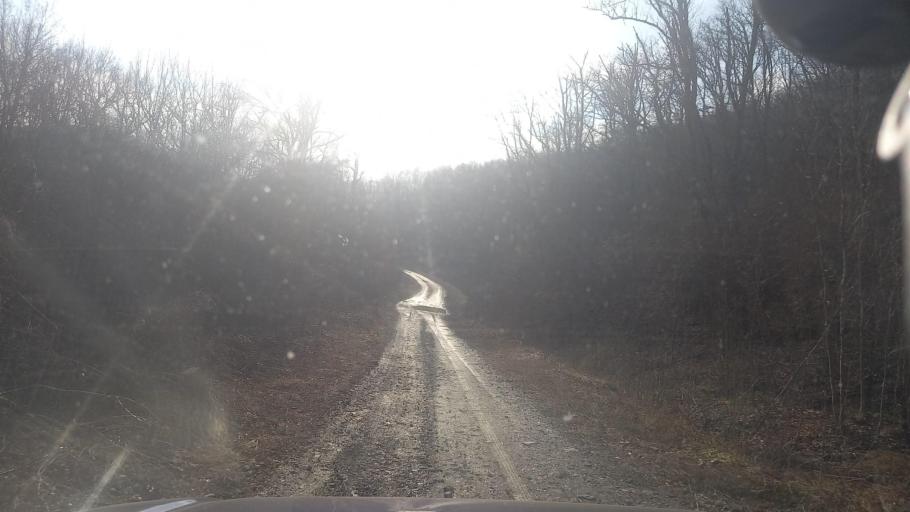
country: RU
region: Krasnodarskiy
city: Smolenskaya
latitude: 44.6845
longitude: 38.7823
